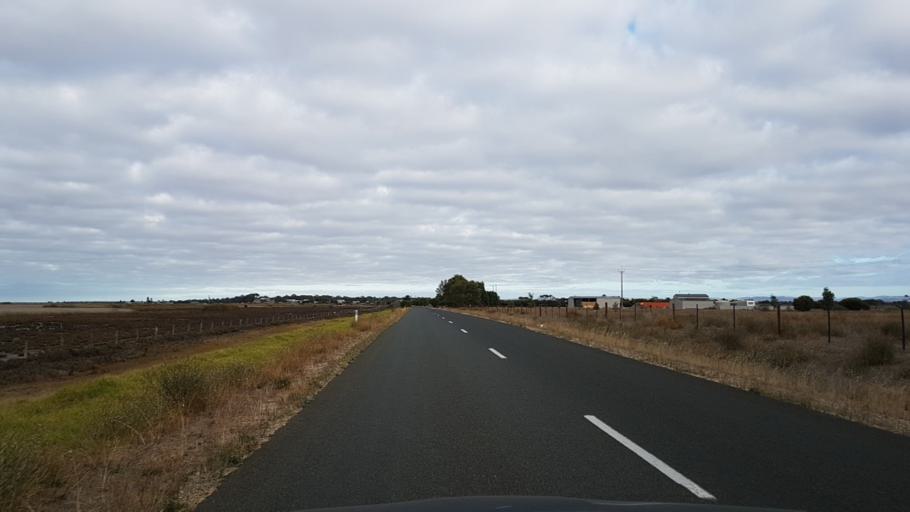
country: AU
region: South Australia
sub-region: Alexandrina
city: Langhorne Creek
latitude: -35.3974
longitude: 138.9941
